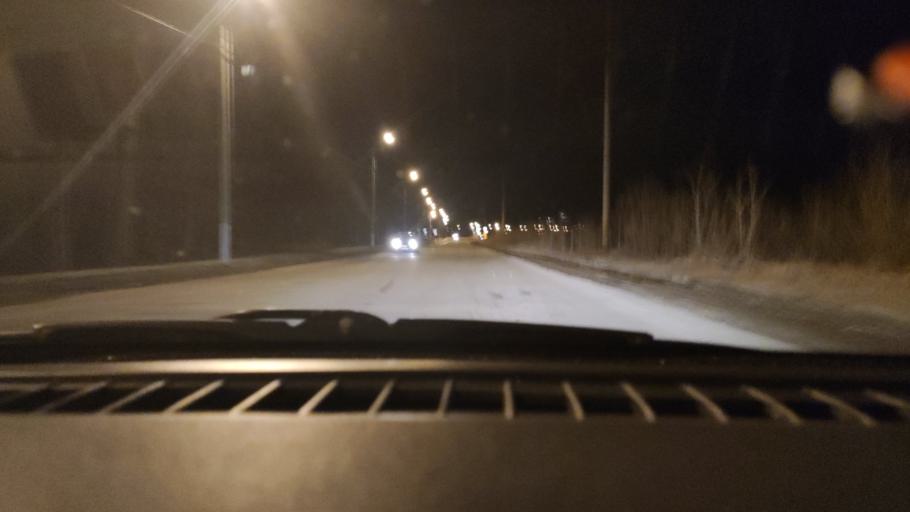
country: RU
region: Perm
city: Perm
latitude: 58.0950
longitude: 56.4023
